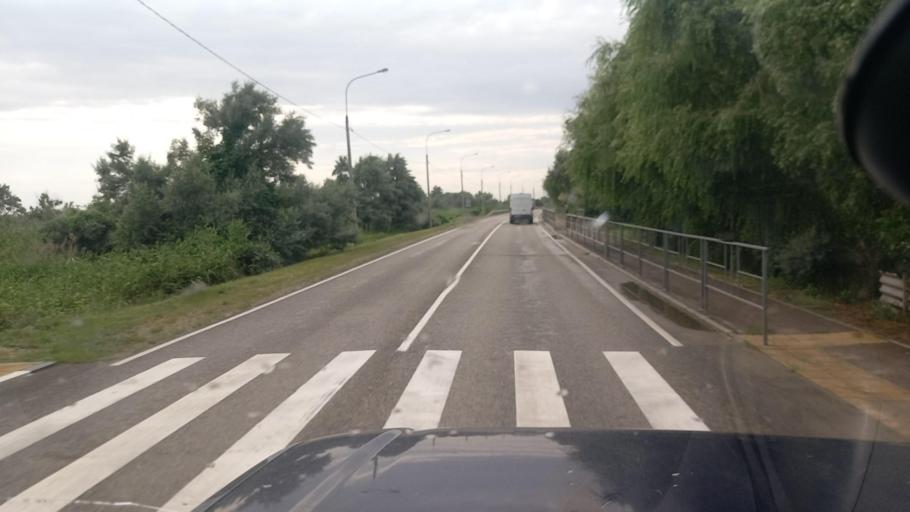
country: RU
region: Krasnodarskiy
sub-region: Taymyrsky Dolgano-Nenetsky District
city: Golubitskaya
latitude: 45.3162
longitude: 37.2903
